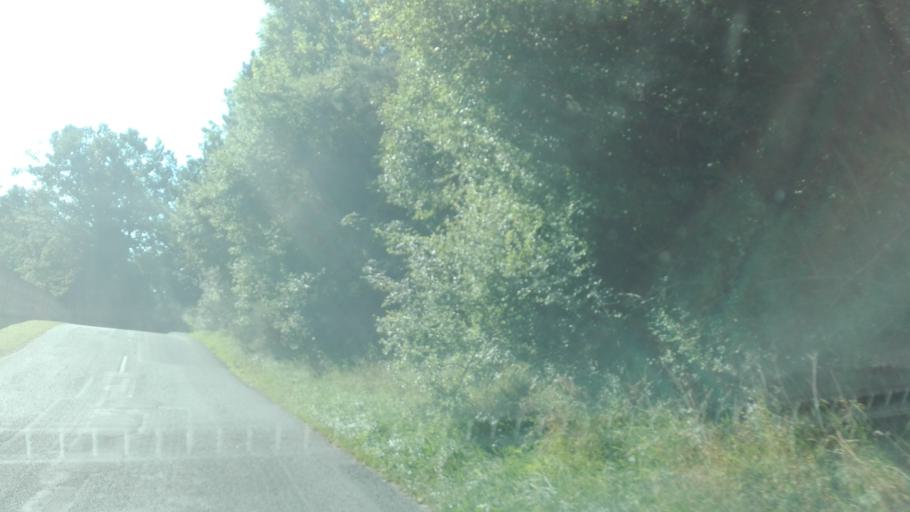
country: DK
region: Central Jutland
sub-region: Syddjurs Kommune
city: Ebeltoft
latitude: 56.2535
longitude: 10.6236
